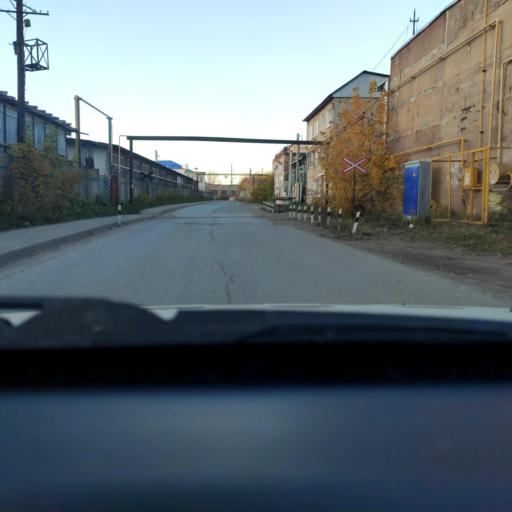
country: RU
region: Perm
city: Kondratovo
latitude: 58.0007
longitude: 56.1514
